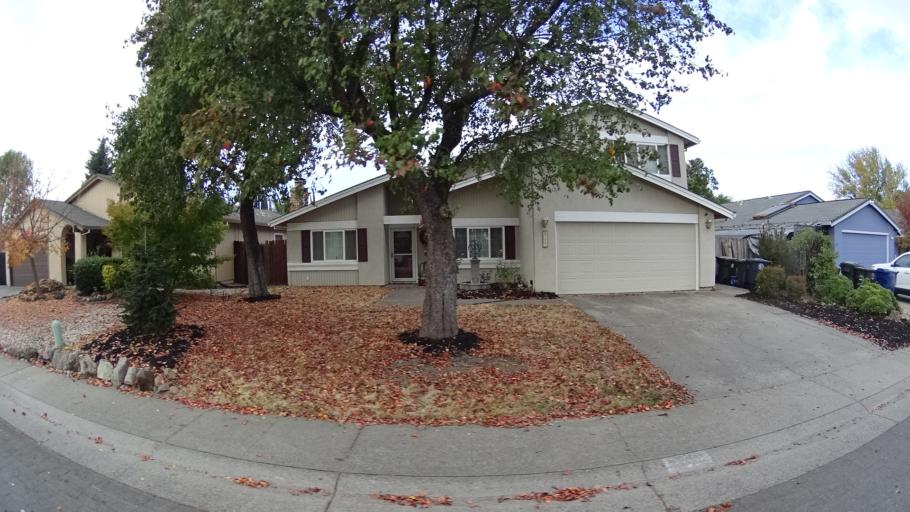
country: US
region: California
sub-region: Sacramento County
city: Citrus Heights
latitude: 38.7143
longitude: -121.2509
